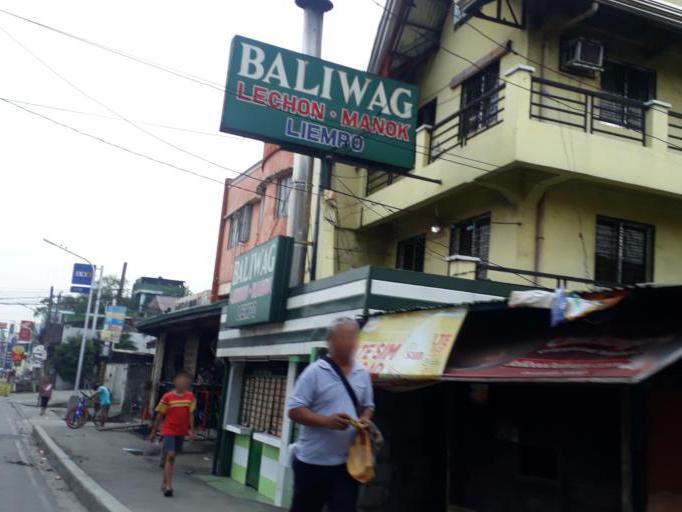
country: PH
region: Metro Manila
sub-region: Caloocan City
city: Niugan
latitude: 14.6596
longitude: 120.9548
